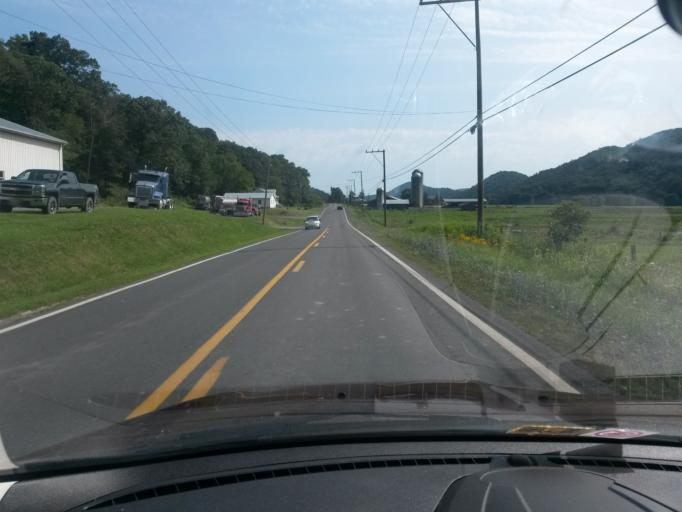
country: US
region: West Virginia
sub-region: Hardy County
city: Moorefield
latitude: 39.0155
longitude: -78.7652
